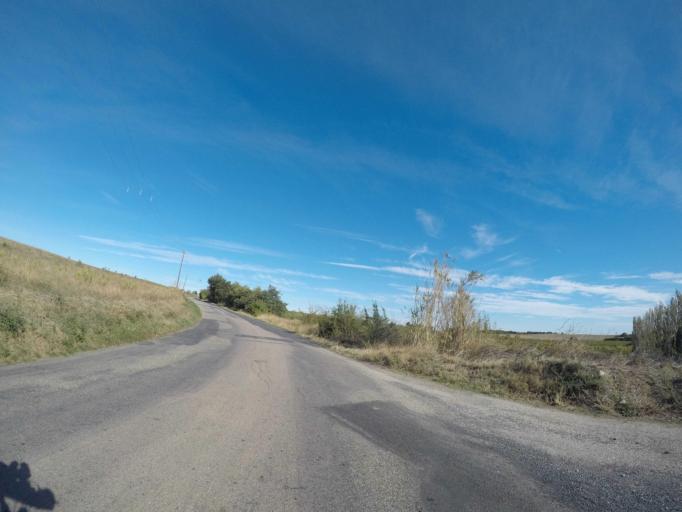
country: FR
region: Languedoc-Roussillon
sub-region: Departement des Pyrenees-Orientales
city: Trouillas
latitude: 42.5971
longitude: 2.8082
